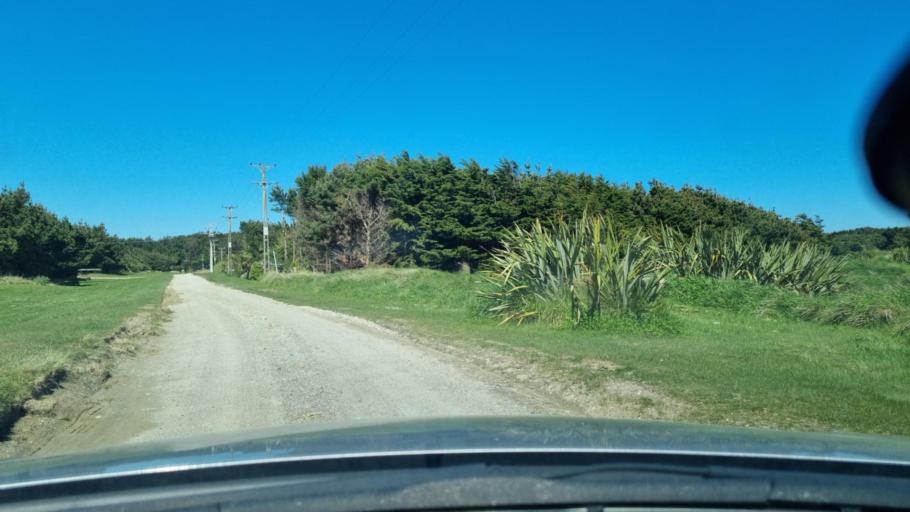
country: NZ
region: Southland
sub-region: Invercargill City
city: Invercargill
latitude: -46.4378
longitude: 168.2386
